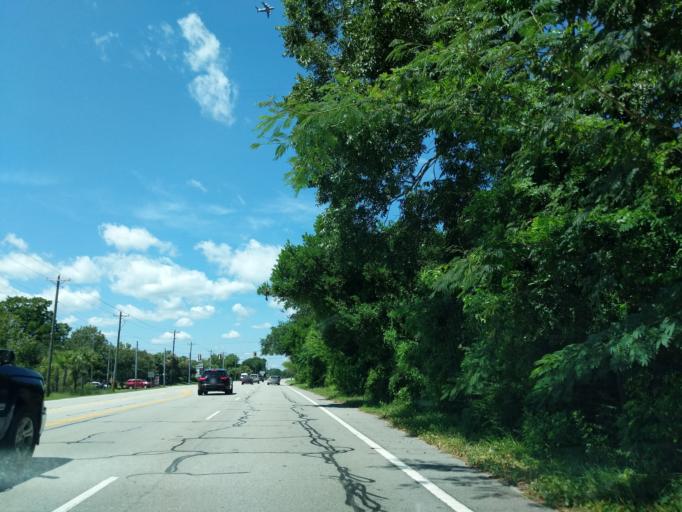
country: US
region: South Carolina
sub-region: Charleston County
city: Folly Beach
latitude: 32.6846
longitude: -79.9587
